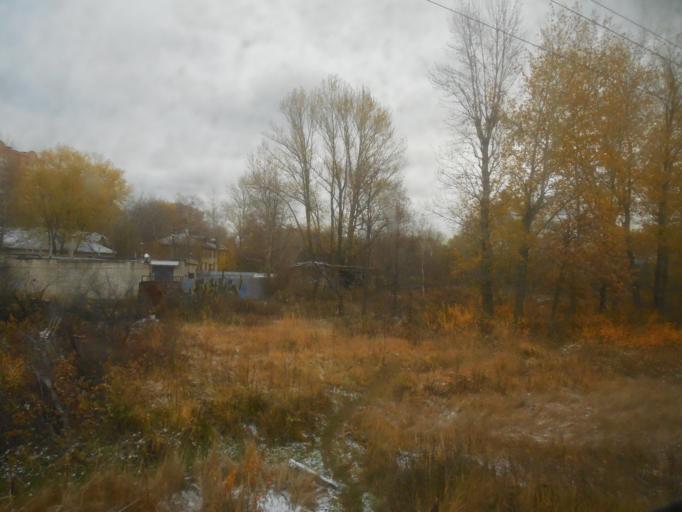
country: RU
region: Moskovskaya
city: Bol'shiye Vyazemy
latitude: 55.6200
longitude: 36.9734
